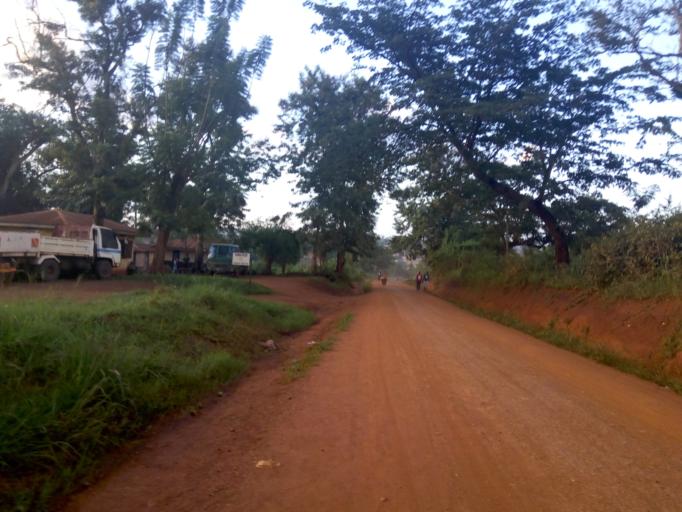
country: UG
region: Western Region
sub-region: Masindi District
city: Masindi
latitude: 1.6756
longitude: 31.7140
